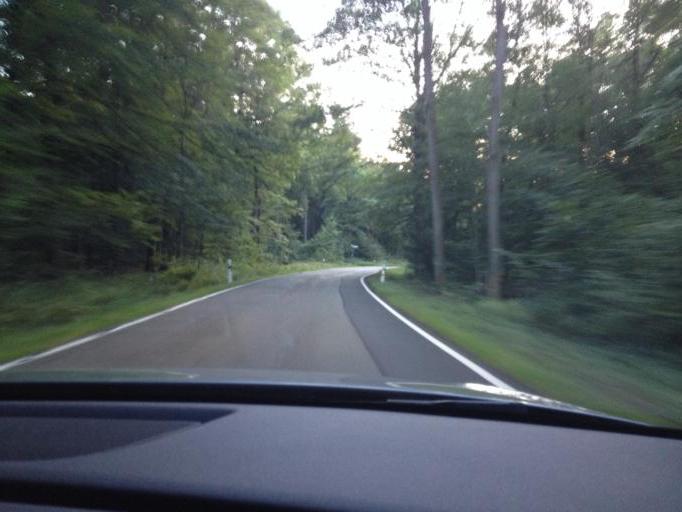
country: DE
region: Rheinland-Pfalz
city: Frohnhofen
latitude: 49.4564
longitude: 7.2874
